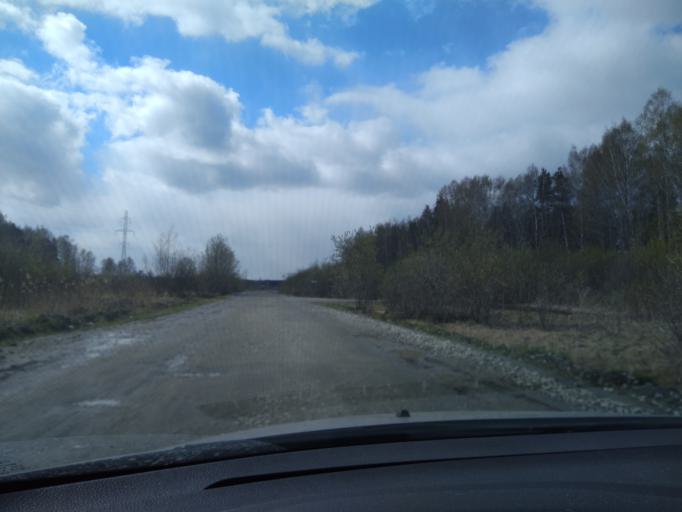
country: RU
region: Sverdlovsk
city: Sredneuralsk
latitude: 56.9709
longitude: 60.4743
